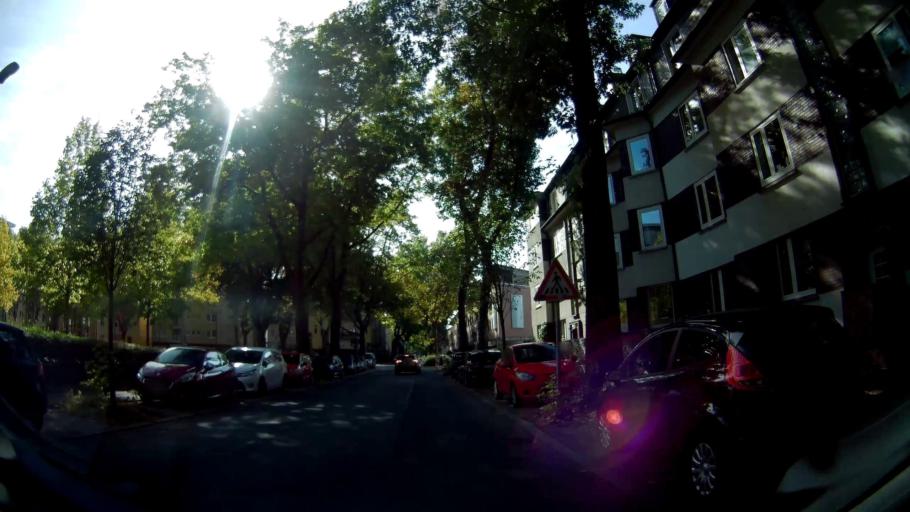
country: DE
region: North Rhine-Westphalia
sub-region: Regierungsbezirk Arnsberg
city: Bochum
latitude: 51.4704
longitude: 7.2129
